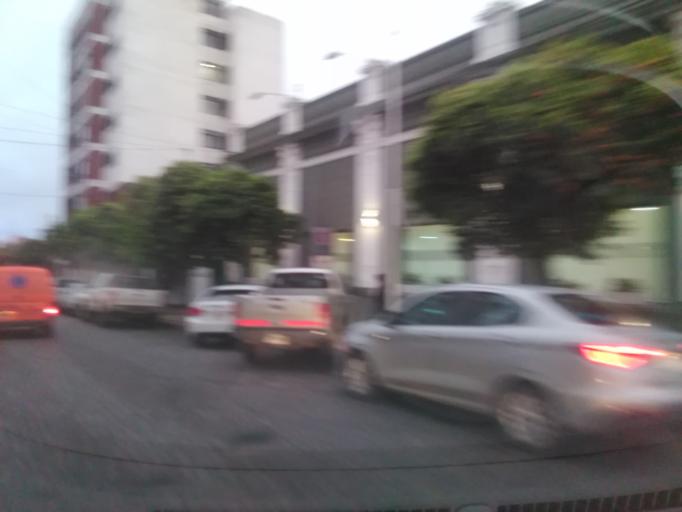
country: AR
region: Buenos Aires
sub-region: Partido de Tandil
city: Tandil
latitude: -37.3257
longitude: -59.1388
